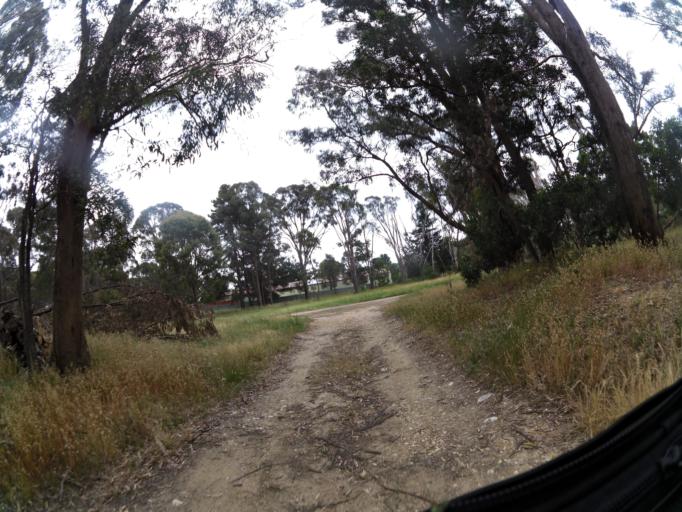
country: AU
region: Victoria
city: Brown Hill
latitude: -37.4356
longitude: 143.9063
